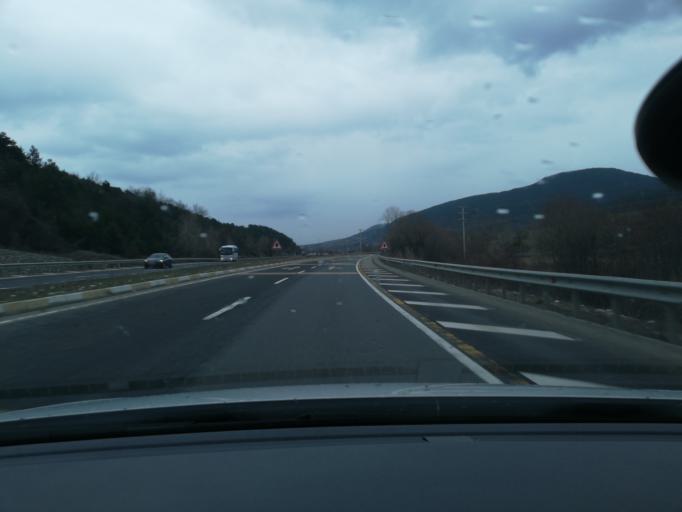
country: TR
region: Bolu
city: Gokcesu
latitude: 40.7417
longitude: 31.8377
